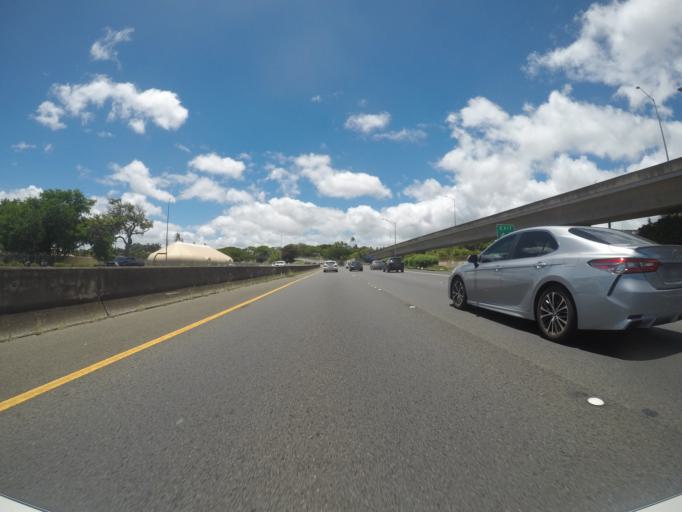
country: US
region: Hawaii
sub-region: Honolulu County
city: Honolulu
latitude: 21.3404
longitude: -157.8855
